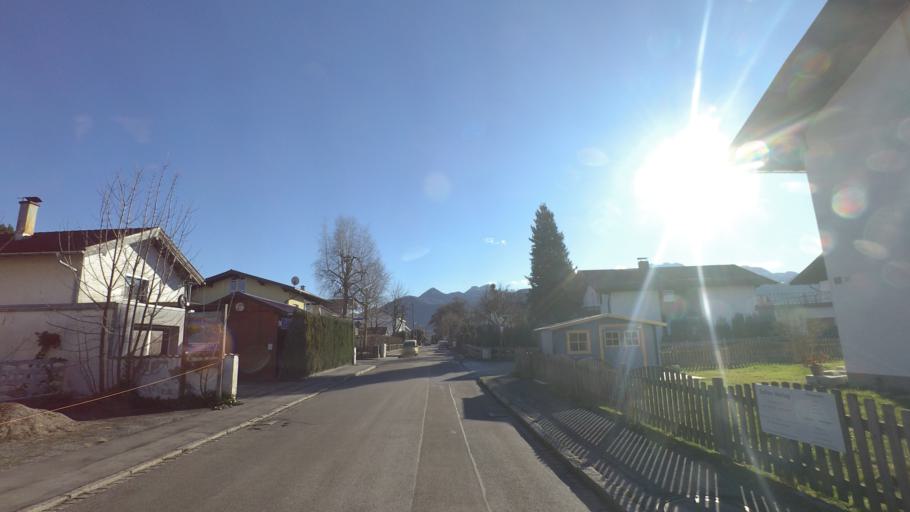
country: DE
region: Bavaria
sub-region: Upper Bavaria
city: Bernau am Chiemsee
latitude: 47.8211
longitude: 12.3851
